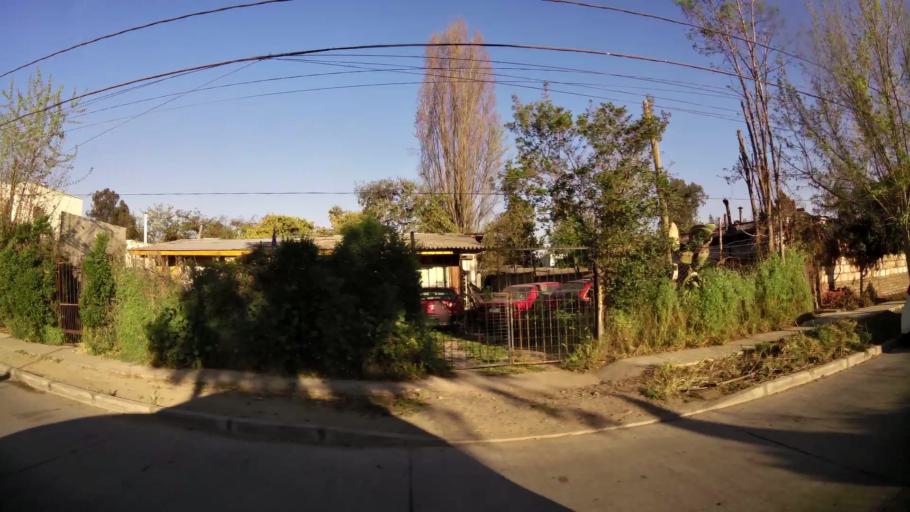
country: CL
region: Santiago Metropolitan
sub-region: Provincia de Talagante
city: Penaflor
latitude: -33.6188
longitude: -70.8657
